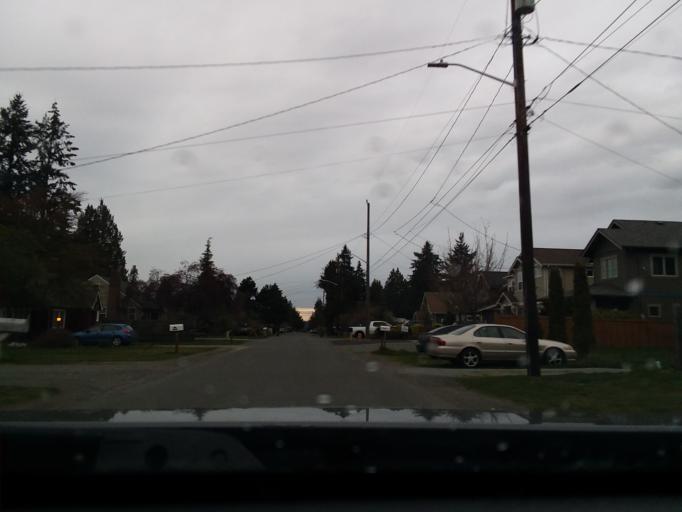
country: US
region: Washington
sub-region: King County
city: Shoreline
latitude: 47.7000
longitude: -122.3741
